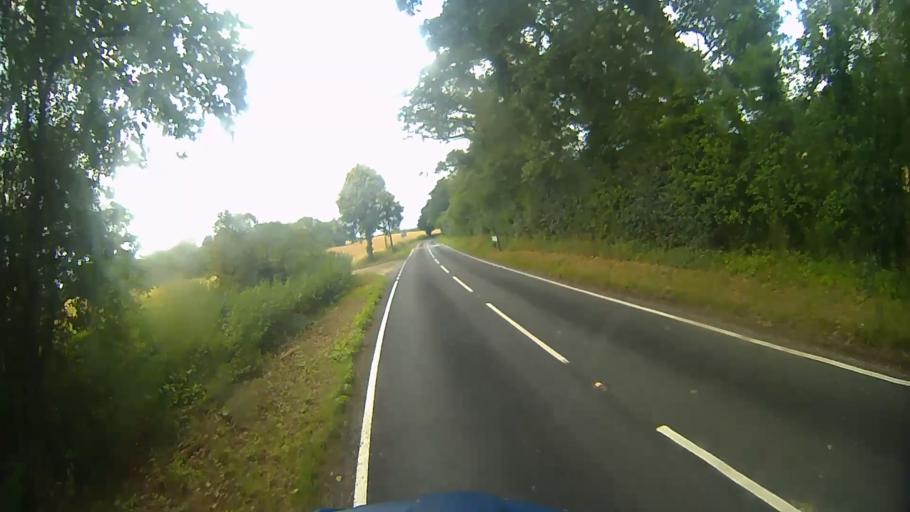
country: GB
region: England
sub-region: Hampshire
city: Four Marks
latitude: 51.1100
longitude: -1.1604
